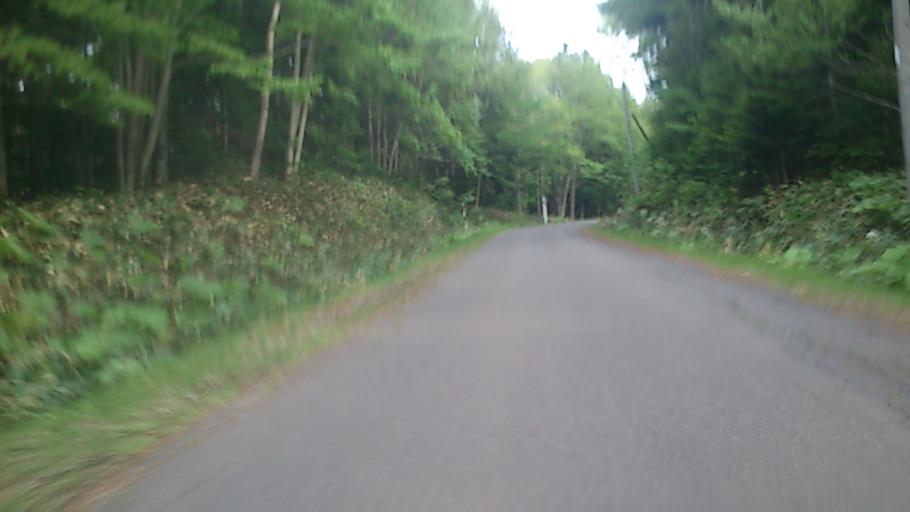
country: JP
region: Hokkaido
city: Bihoro
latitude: 43.4280
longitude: 144.0847
